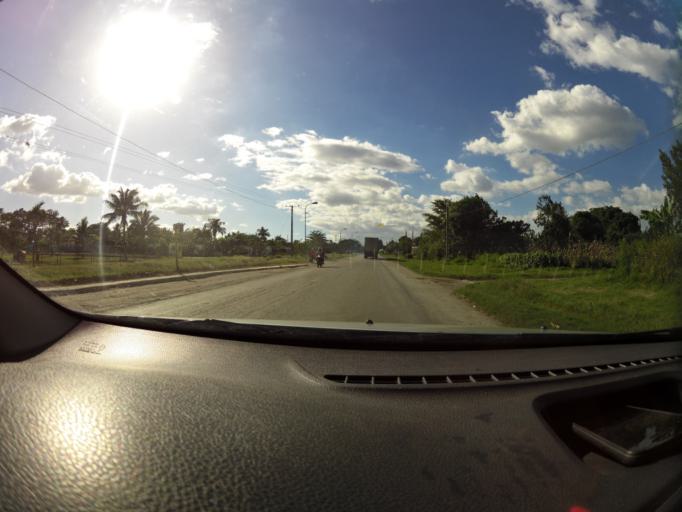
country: CU
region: Santiago de Cuba
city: Palma Soriano
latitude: 20.2320
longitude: -76.0150
